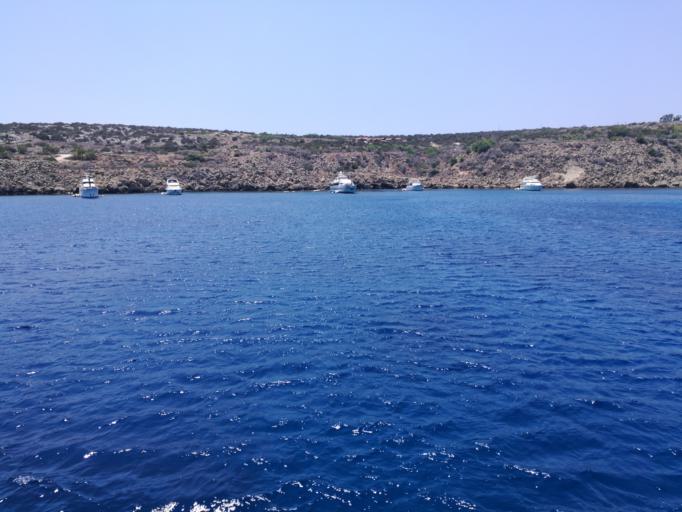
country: CY
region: Ammochostos
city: Protaras
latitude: 34.9778
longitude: 34.0759
